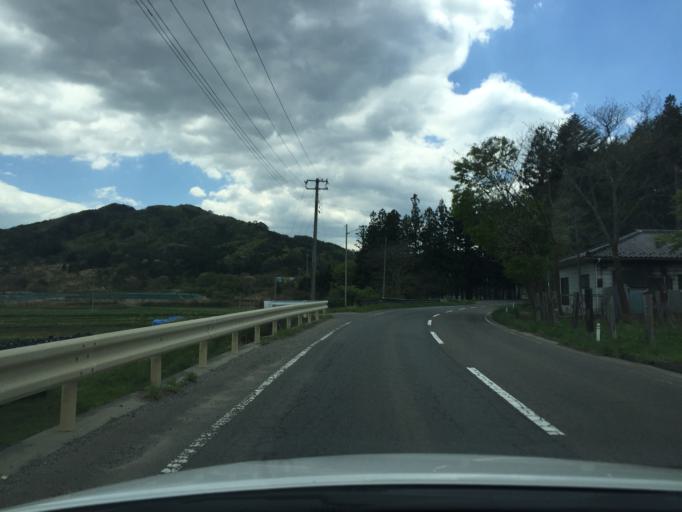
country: JP
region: Fukushima
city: Yanagawamachi-saiwaicho
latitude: 37.7185
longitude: 140.6905
